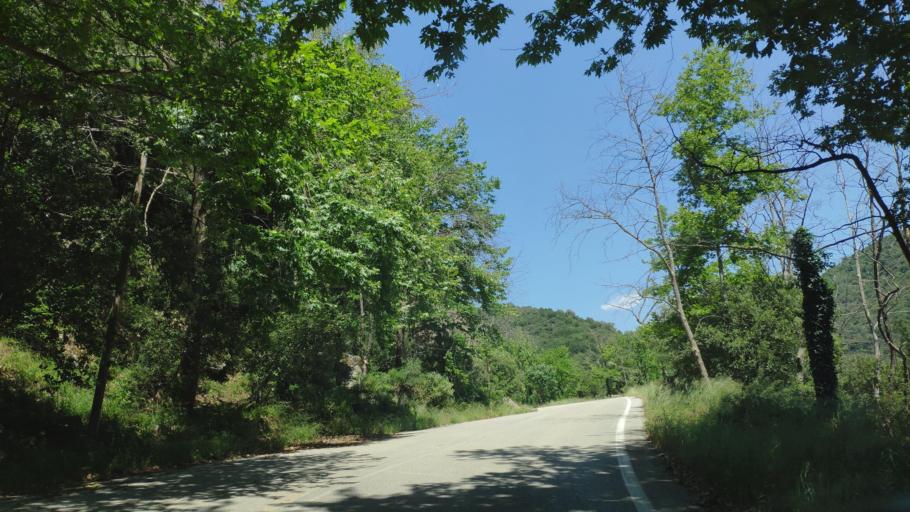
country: GR
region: West Greece
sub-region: Nomos Aitolias kai Akarnanias
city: Sardinia
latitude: 38.9230
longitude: 21.3585
